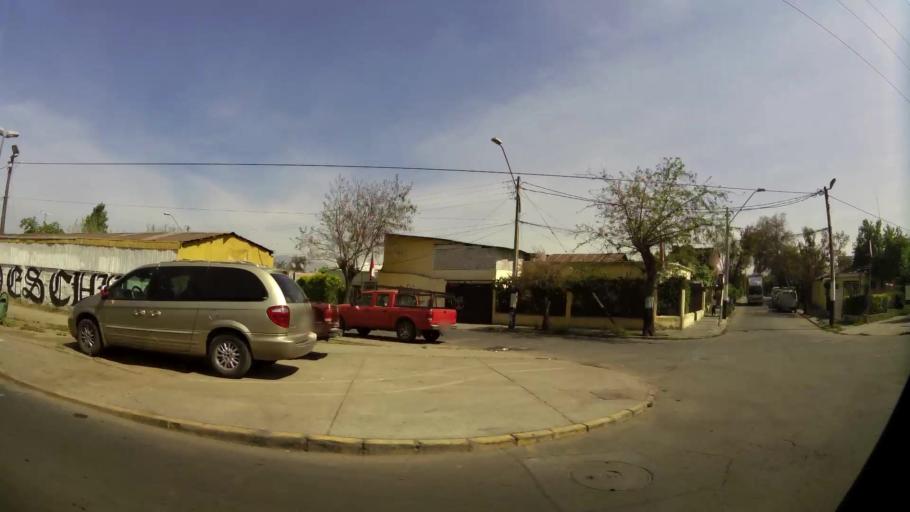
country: CL
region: Santiago Metropolitan
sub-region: Provincia de Santiago
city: Lo Prado
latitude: -33.4411
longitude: -70.7310
